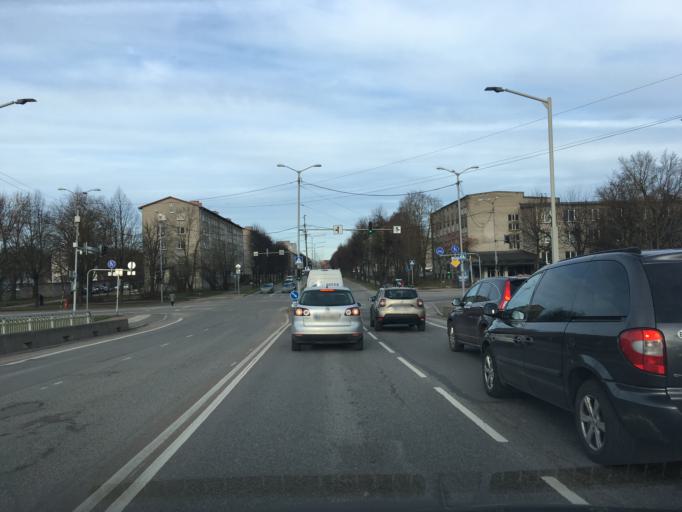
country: EE
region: Ida-Virumaa
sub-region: Narva linn
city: Narva
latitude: 59.3736
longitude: 28.1827
